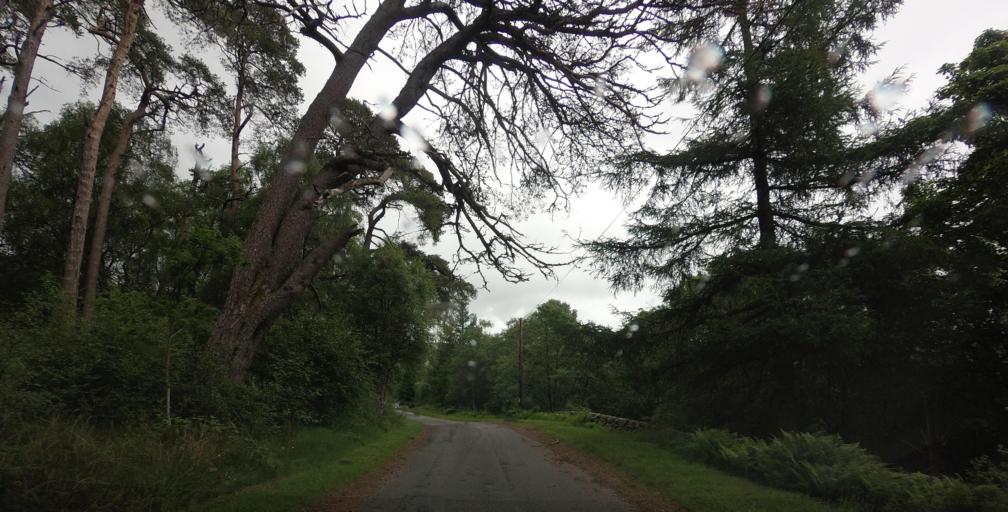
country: GB
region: Scotland
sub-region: Highland
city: Fort William
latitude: 56.8560
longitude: -5.2507
